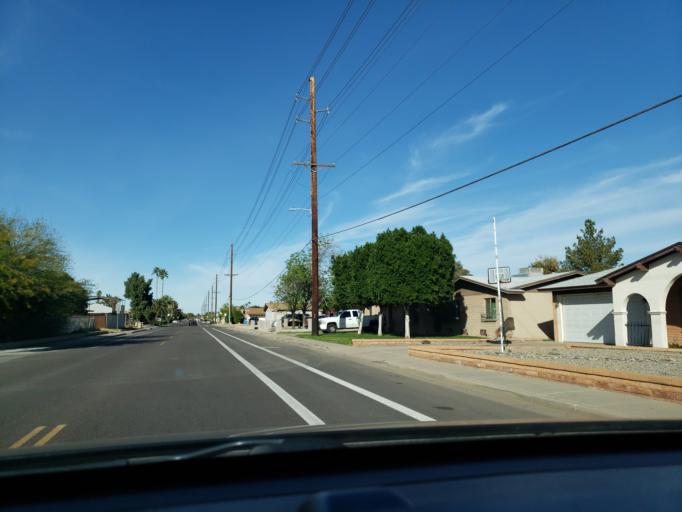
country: US
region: Arizona
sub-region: Maricopa County
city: Glendale
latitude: 33.5690
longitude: -112.1429
